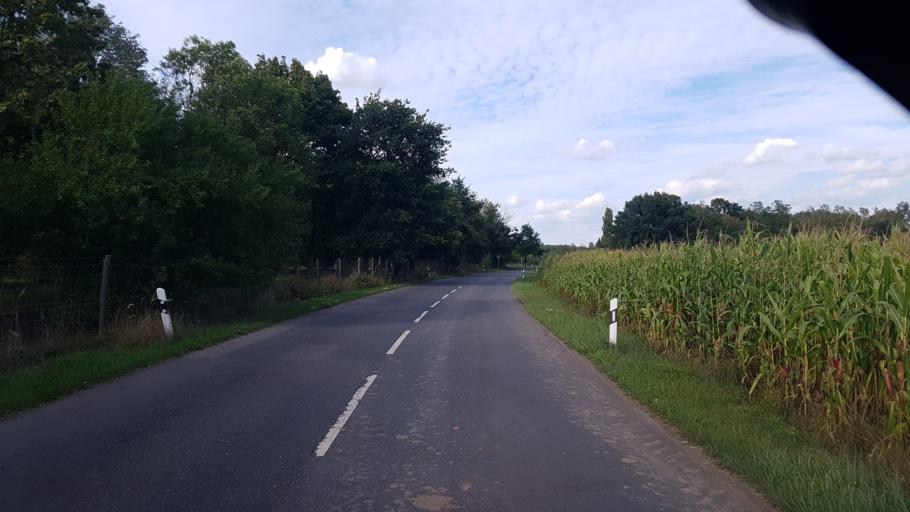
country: DE
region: Brandenburg
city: Spremberg
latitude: 51.5544
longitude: 14.3187
